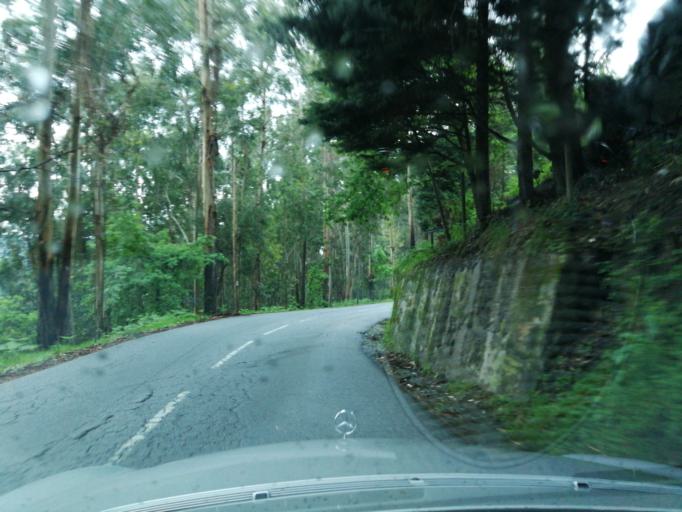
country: PT
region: Braga
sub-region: Vila Nova de Famalicao
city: Joane
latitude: 41.4712
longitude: -8.4284
